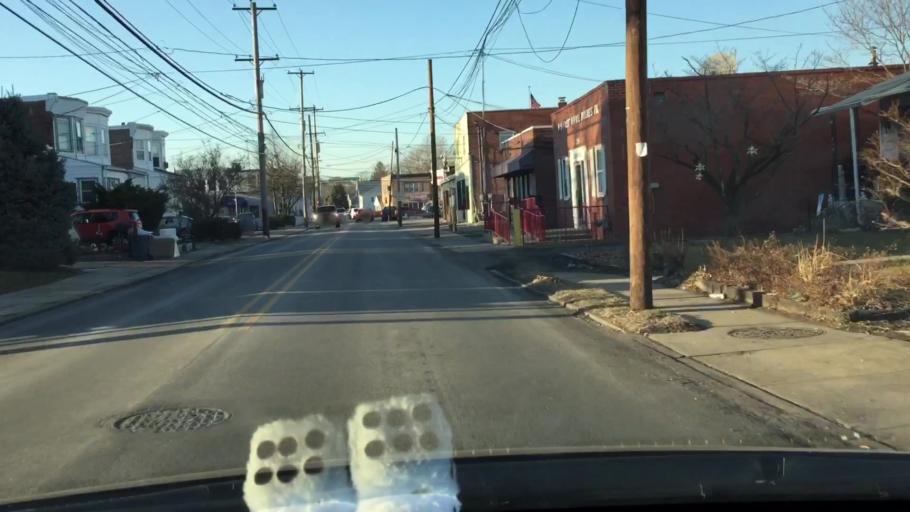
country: US
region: Pennsylvania
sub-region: Delaware County
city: Prospect Park
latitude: 39.8973
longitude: -75.3073
